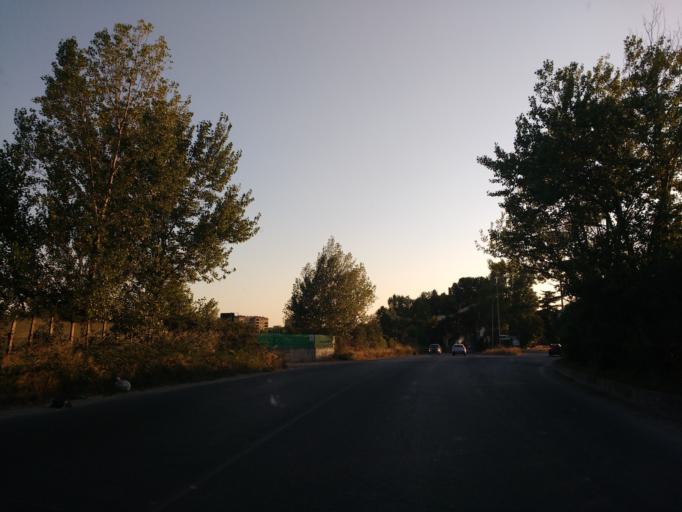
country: IT
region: Latium
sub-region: Citta metropolitana di Roma Capitale
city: Villalba
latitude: 41.9534
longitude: 12.7403
